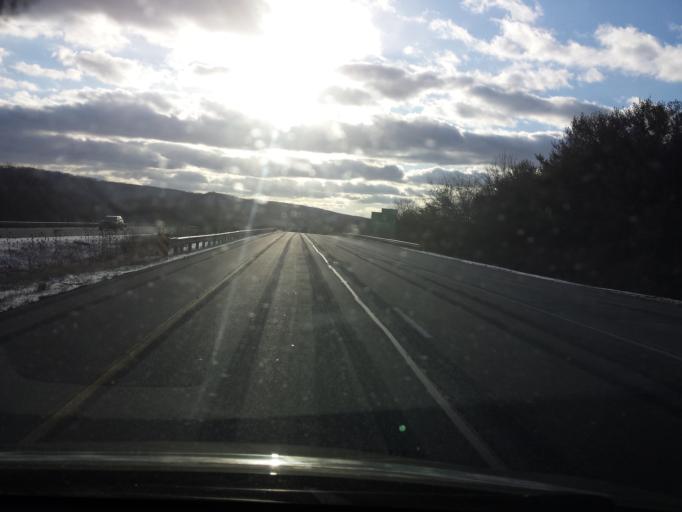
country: US
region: Pennsylvania
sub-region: Northumberland County
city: Riverside
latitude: 40.9970
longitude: -76.6435
